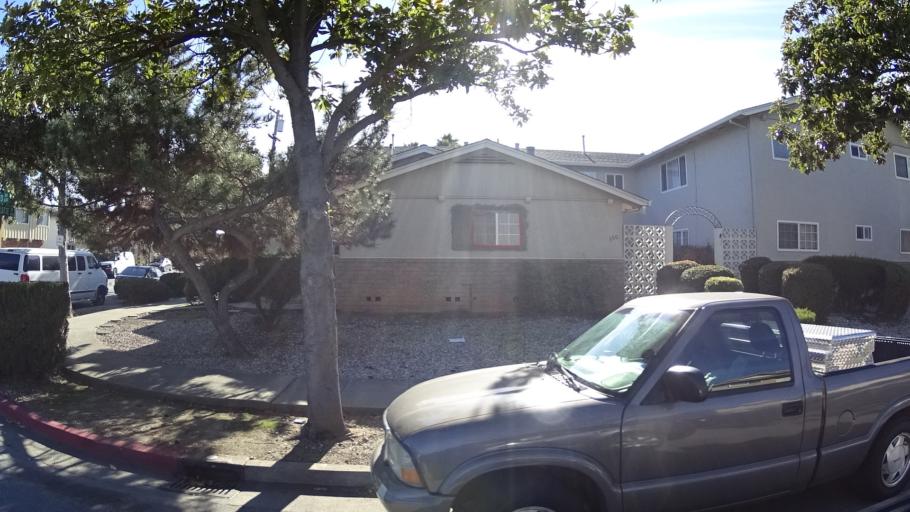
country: US
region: California
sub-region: Santa Clara County
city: Cupertino
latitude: 37.3407
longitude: -122.0379
